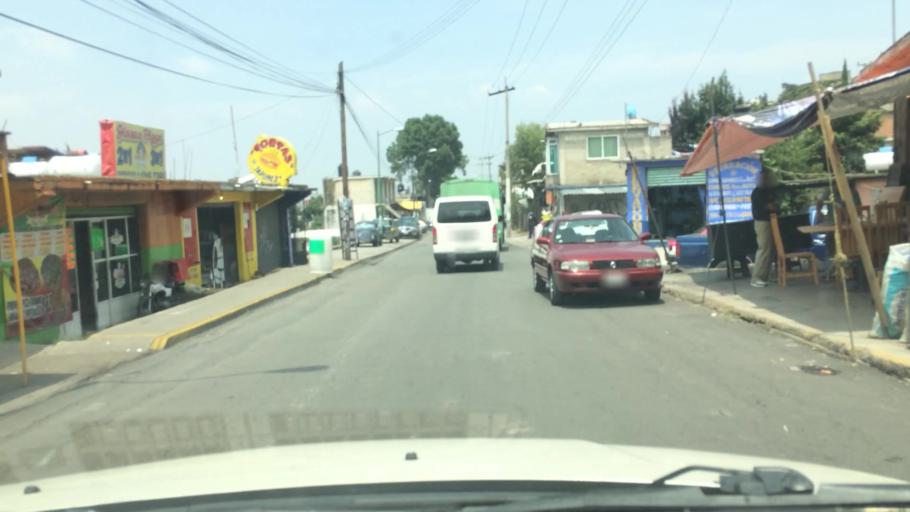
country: MX
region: Mexico City
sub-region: Tlalpan
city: Lomas de Tepemecatl
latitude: 19.2328
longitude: -99.1781
